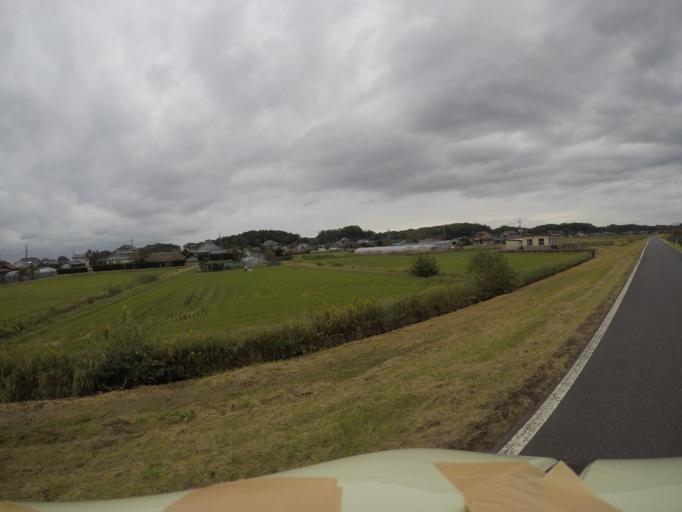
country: JP
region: Ibaraki
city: Inashiki
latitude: 36.0917
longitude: 140.3844
